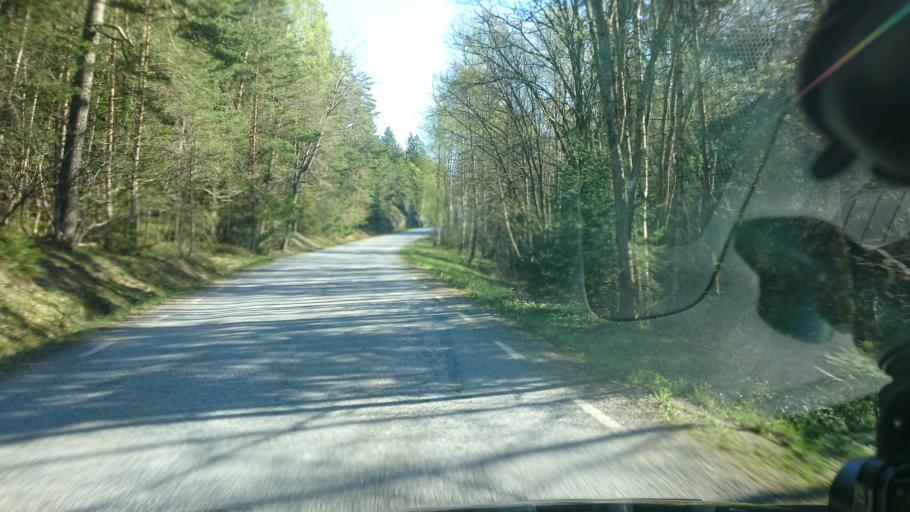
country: SE
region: Vaestra Goetaland
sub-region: Munkedals Kommun
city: Munkedal
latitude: 58.4020
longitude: 11.6571
